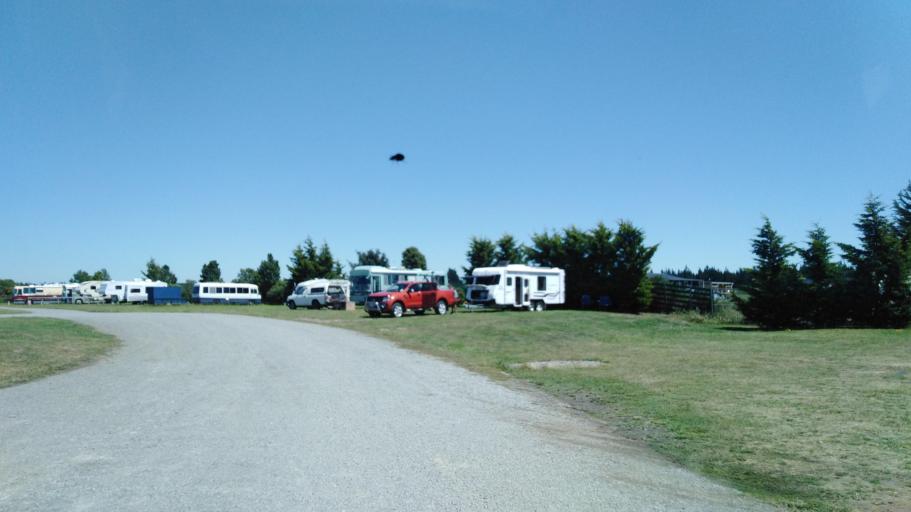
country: NZ
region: Canterbury
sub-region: Selwyn District
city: Rolleston
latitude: -43.5633
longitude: 172.4368
